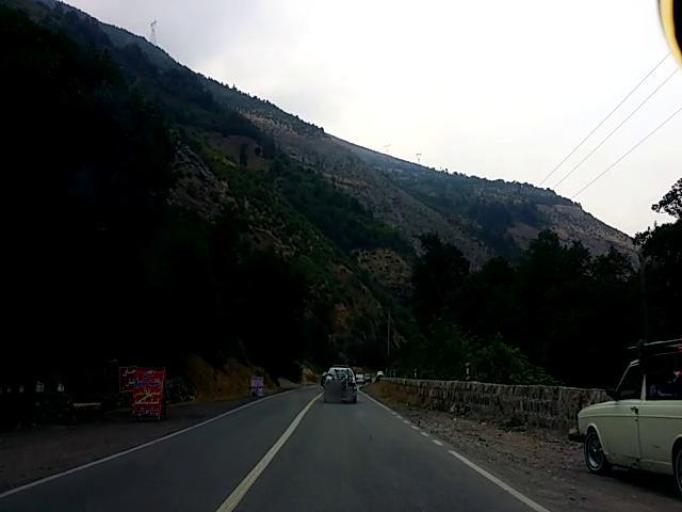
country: IR
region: Mazandaran
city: Chalus
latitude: 36.3626
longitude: 51.2618
